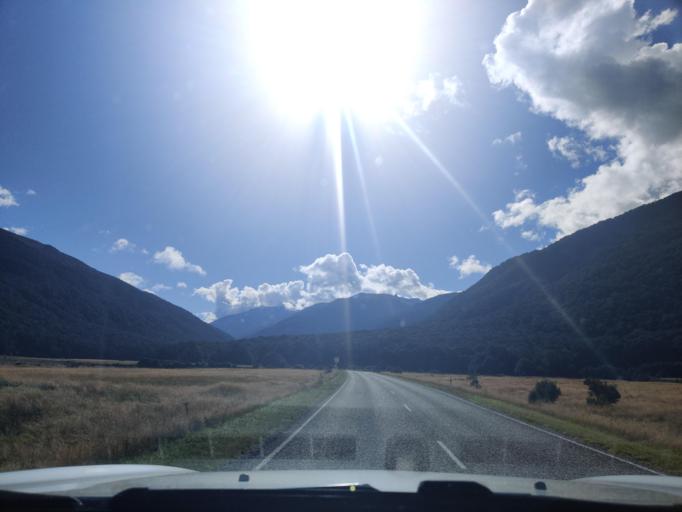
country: NZ
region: Otago
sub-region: Queenstown-Lakes District
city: Wanaka
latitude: -44.1573
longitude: 169.2977
